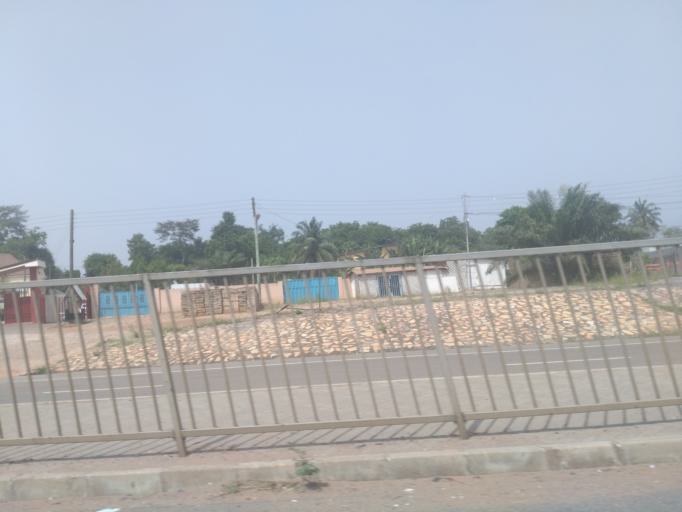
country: GH
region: Greater Accra
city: Dome
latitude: 5.6169
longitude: -0.2000
